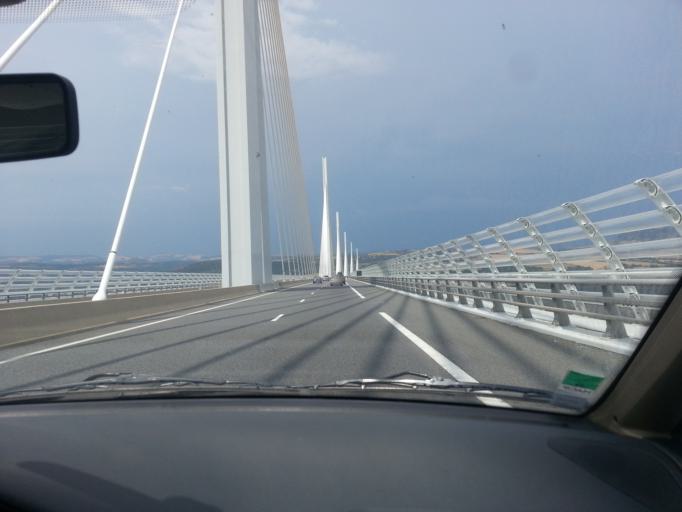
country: FR
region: Midi-Pyrenees
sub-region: Departement de l'Aveyron
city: Saint-Georges-de-Luzencon
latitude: 44.0733
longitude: 3.0239
